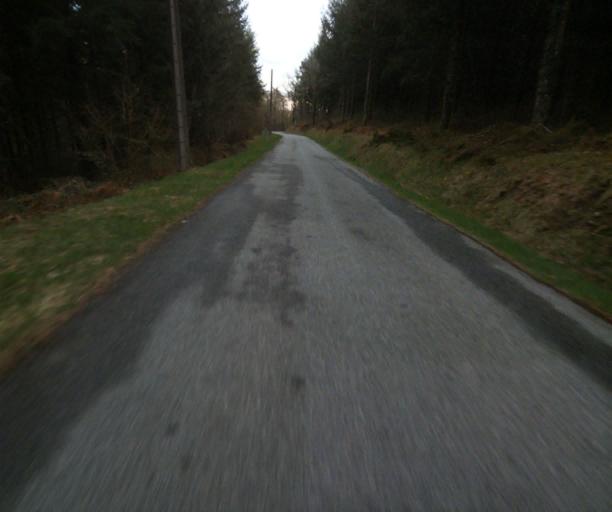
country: FR
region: Limousin
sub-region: Departement de la Correze
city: Correze
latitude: 45.2530
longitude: 1.9813
